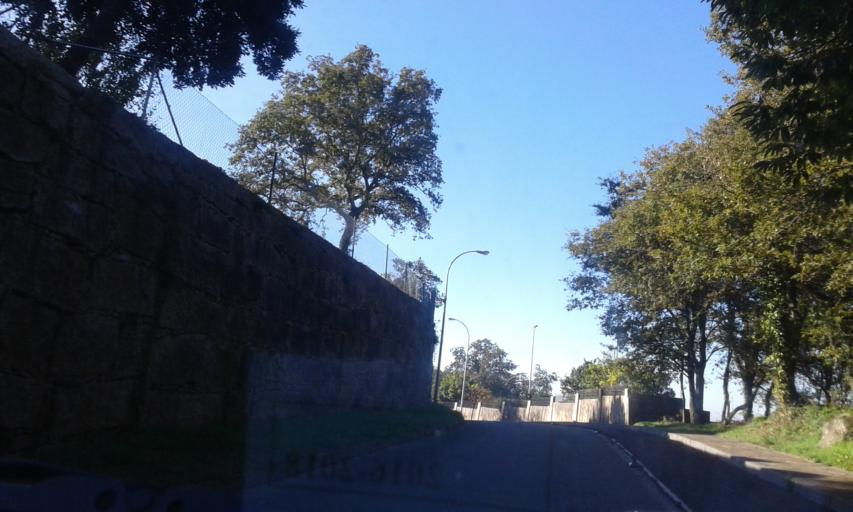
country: ES
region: Galicia
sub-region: Provincia de Pontevedra
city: Marin
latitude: 42.3806
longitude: -8.7256
